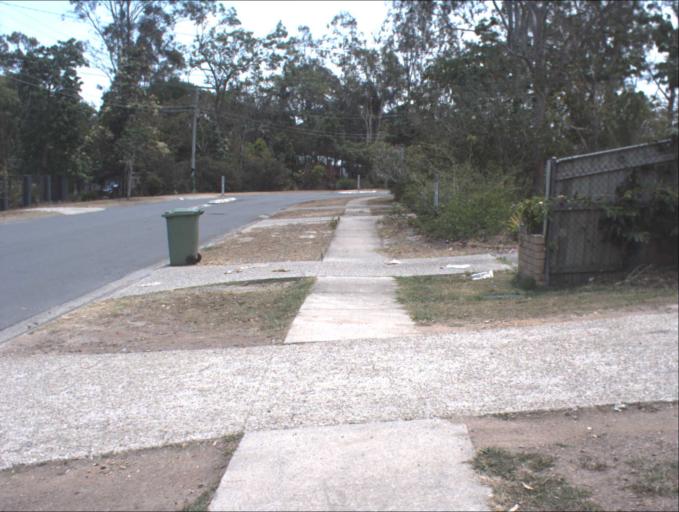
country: AU
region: Queensland
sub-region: Logan
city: Slacks Creek
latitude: -27.6692
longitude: 153.1820
